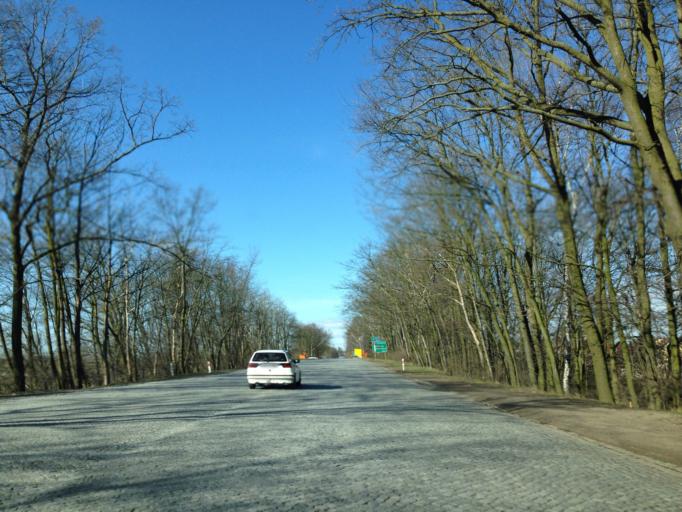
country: PL
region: Pomeranian Voivodeship
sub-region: Powiat tczewski
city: Tczew
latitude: 54.0480
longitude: 18.7698
